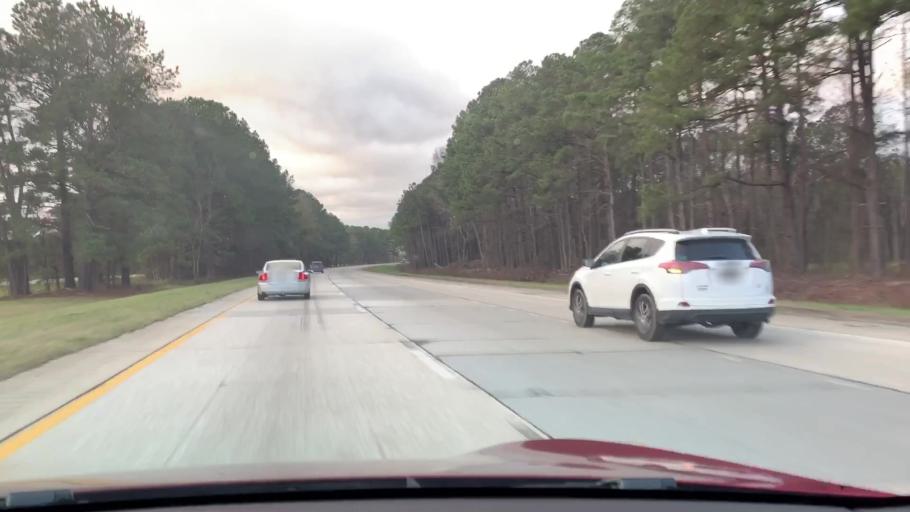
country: US
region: South Carolina
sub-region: Dillon County
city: Dillon
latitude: 34.4155
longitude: -79.4169
